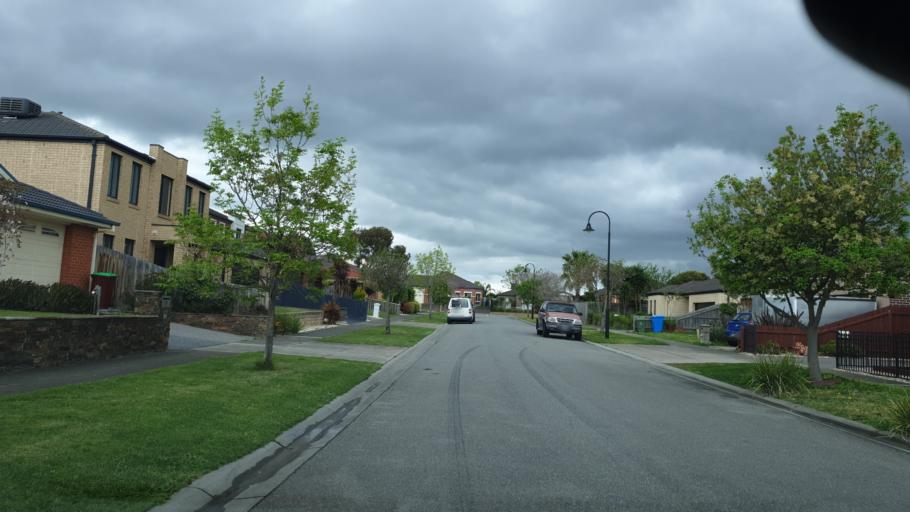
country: AU
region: Victoria
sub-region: Casey
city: Cranbourne North
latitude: -38.0682
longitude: 145.2947
